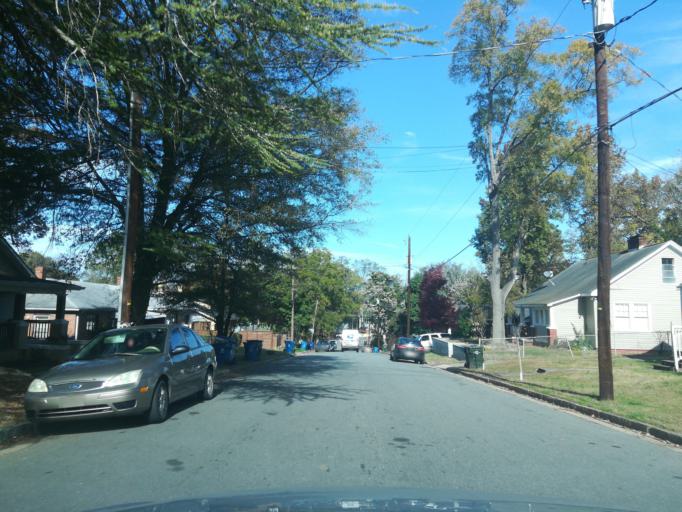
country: US
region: North Carolina
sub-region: Durham County
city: Durham
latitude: 35.9912
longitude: -78.8806
